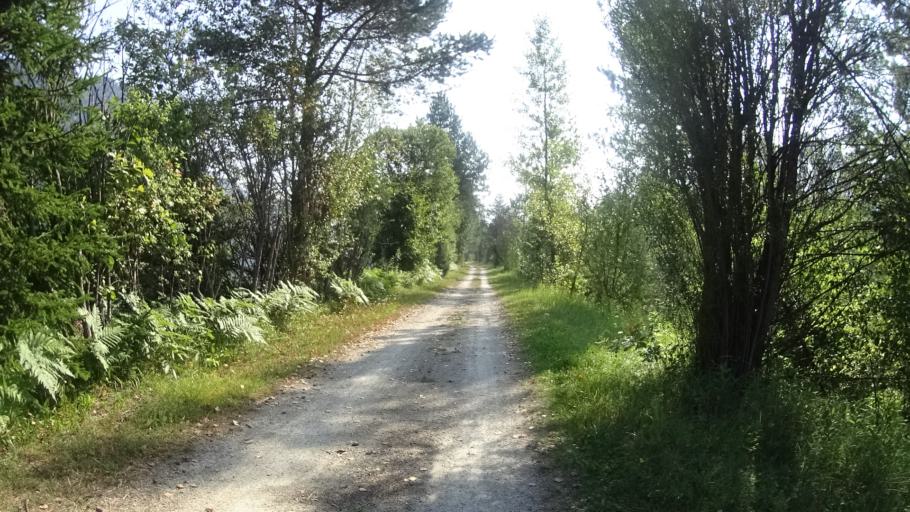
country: AT
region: Carinthia
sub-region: Politischer Bezirk Klagenfurt Land
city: Ebenthal
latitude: 46.5454
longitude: 14.3625
